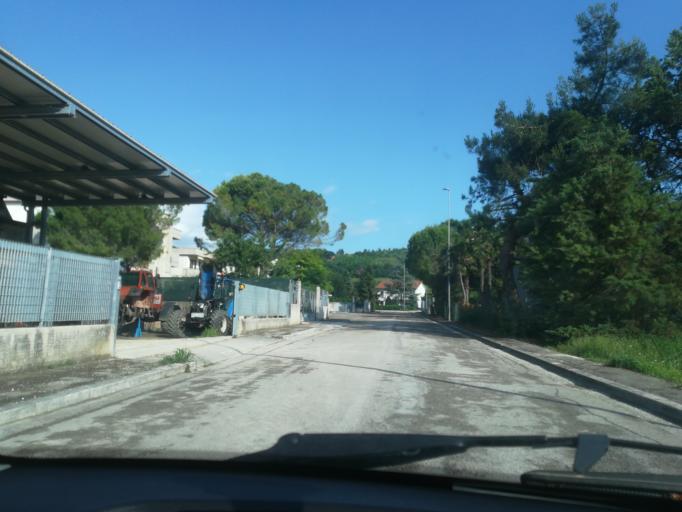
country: IT
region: The Marches
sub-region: Provincia di Macerata
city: Villa Potenza
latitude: 43.3166
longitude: 13.4186
